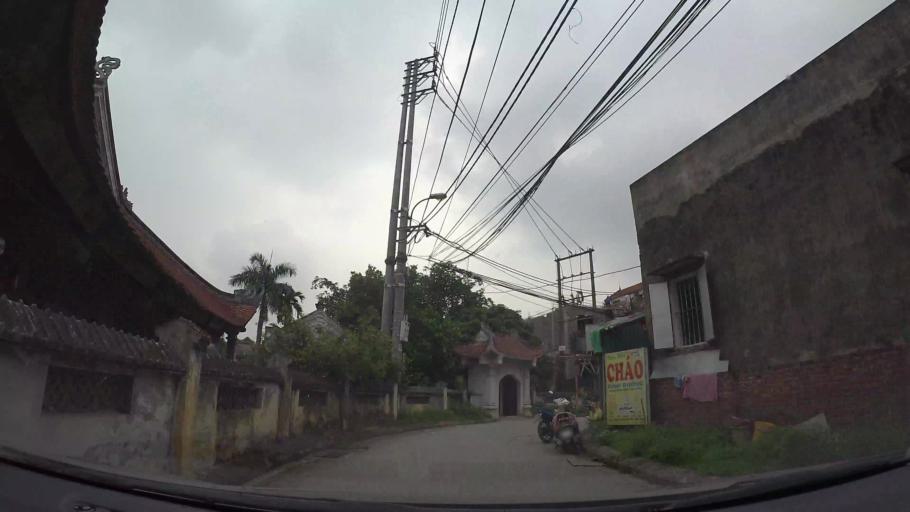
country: VN
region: Ha Noi
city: Trau Quy
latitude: 21.0720
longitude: 105.9182
